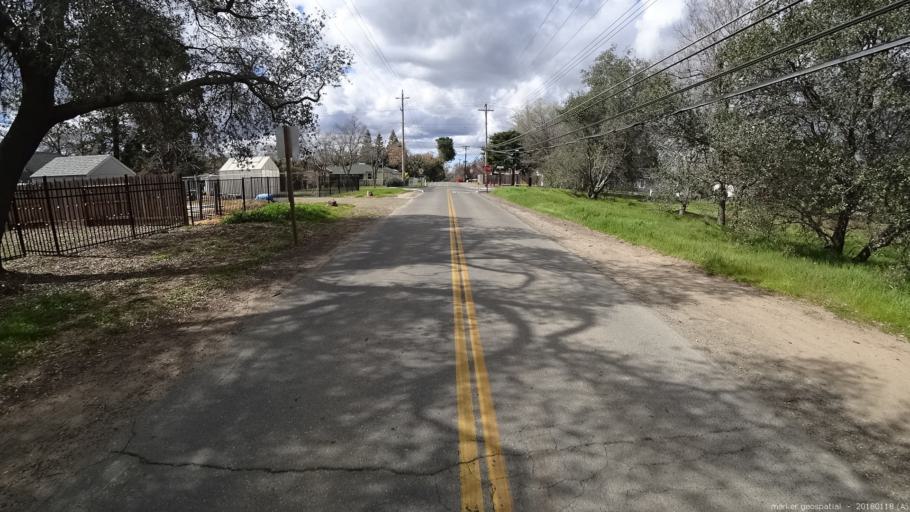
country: US
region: California
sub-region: Sacramento County
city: Orangevale
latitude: 38.6928
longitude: -121.2107
